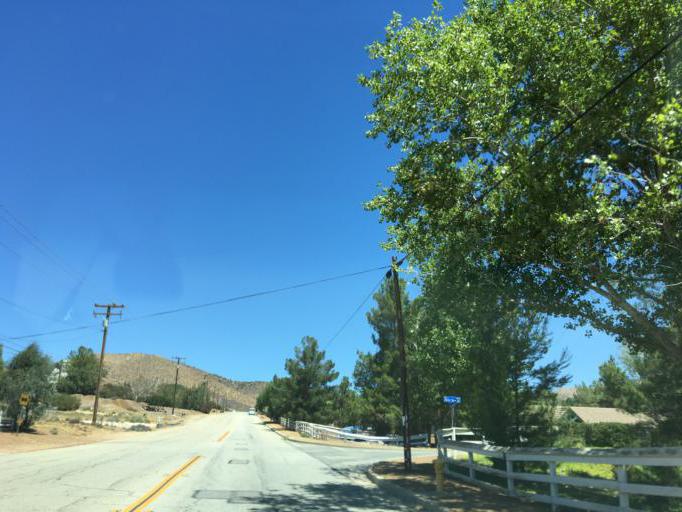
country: US
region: California
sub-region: Los Angeles County
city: Acton
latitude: 34.5009
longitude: -118.1983
